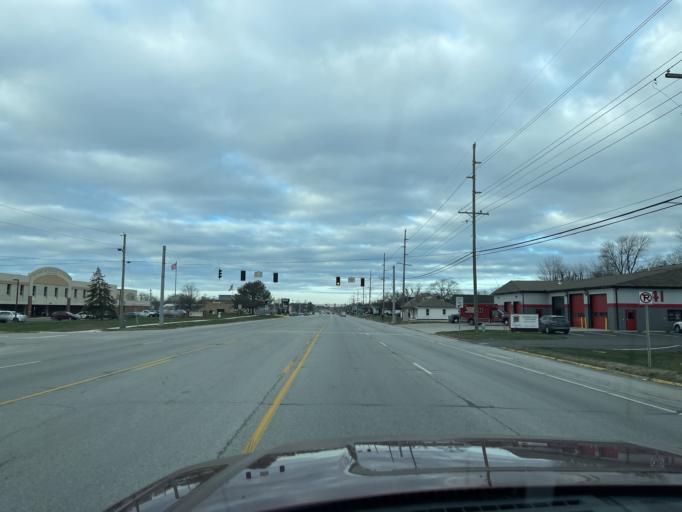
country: US
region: Indiana
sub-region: Hendricks County
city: Avon
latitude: 39.7629
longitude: -86.3947
